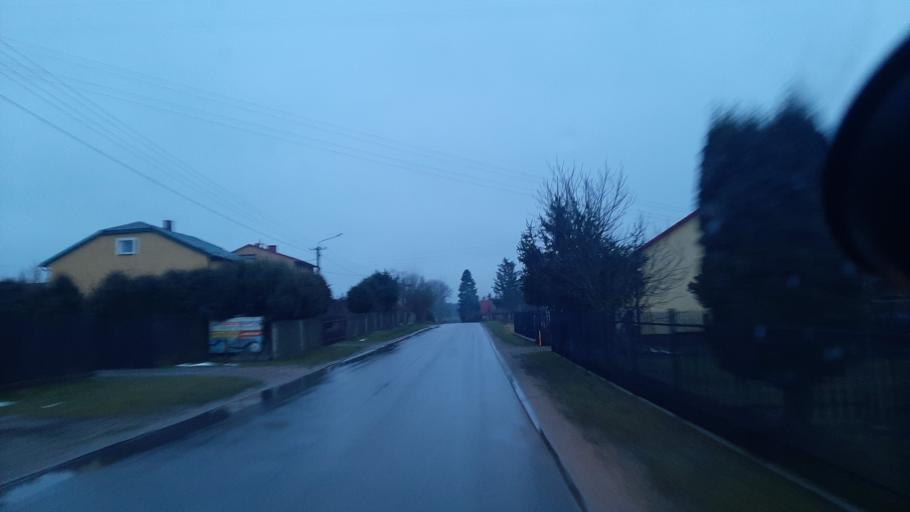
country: PL
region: Lublin Voivodeship
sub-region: Powiat lubartowski
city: Kamionka
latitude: 51.4034
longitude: 22.4140
